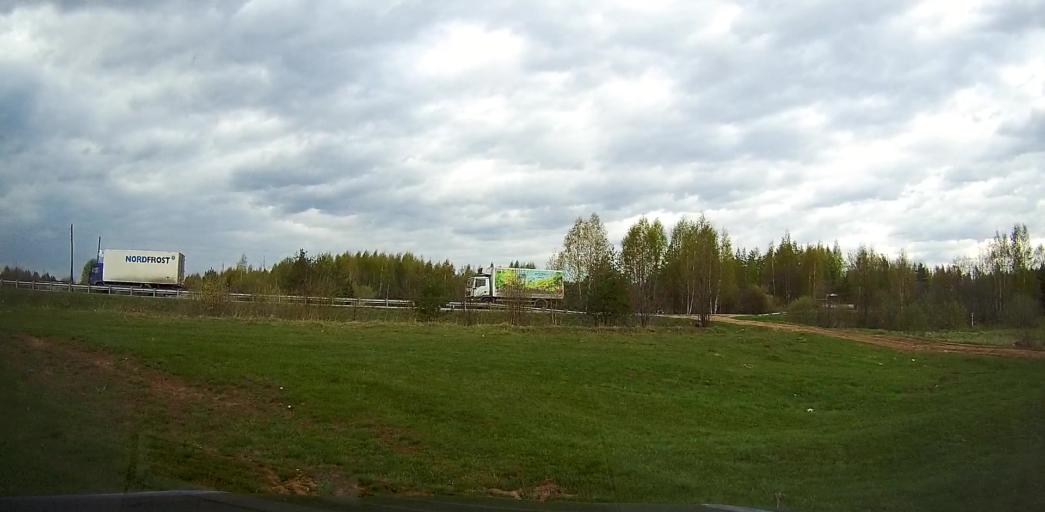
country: RU
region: Moskovskaya
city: Pavlovskiy Posad
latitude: 55.8021
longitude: 38.6713
